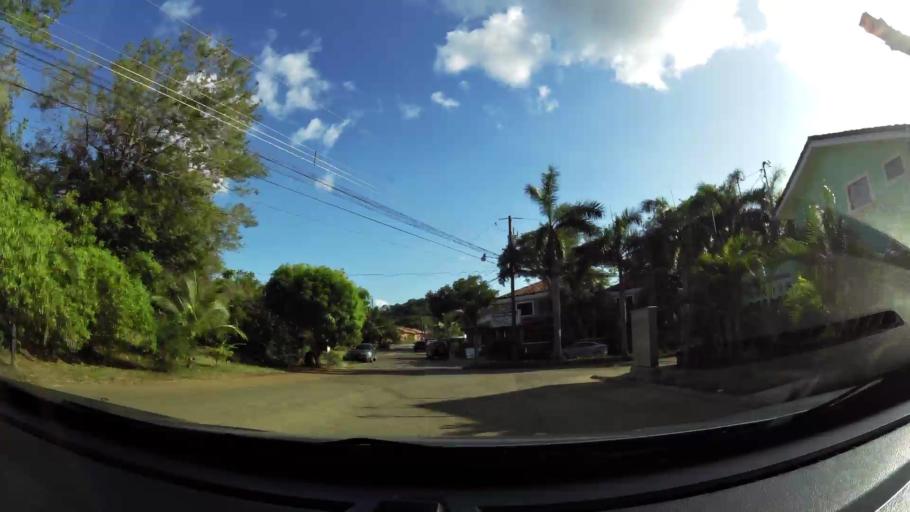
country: CR
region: Guanacaste
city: Sardinal
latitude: 10.5548
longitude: -85.6916
